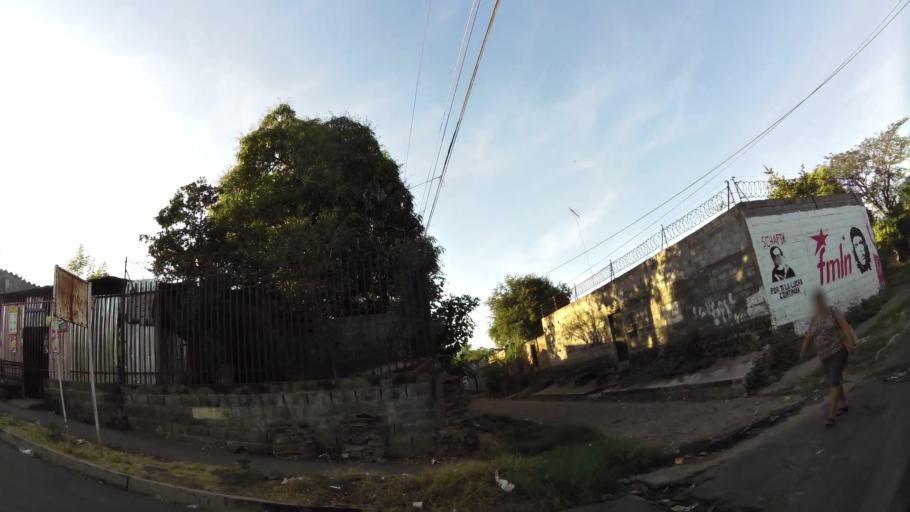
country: SV
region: San Miguel
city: San Miguel
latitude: 13.4703
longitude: -88.1632
